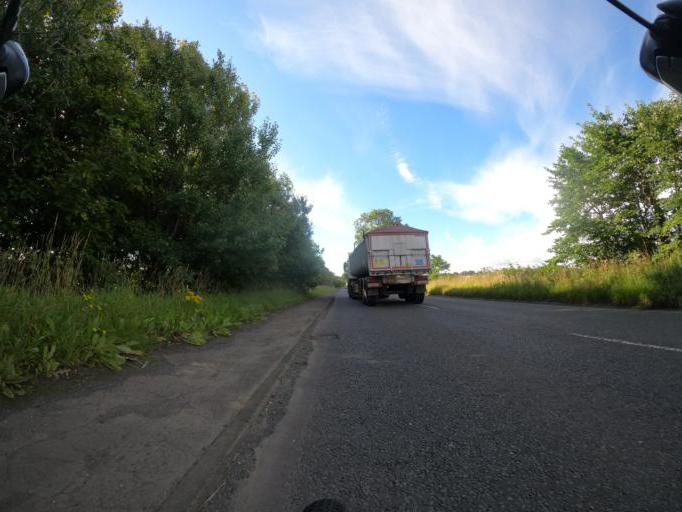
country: GB
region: Scotland
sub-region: Edinburgh
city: Newbridge
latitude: 55.9208
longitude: -3.4112
